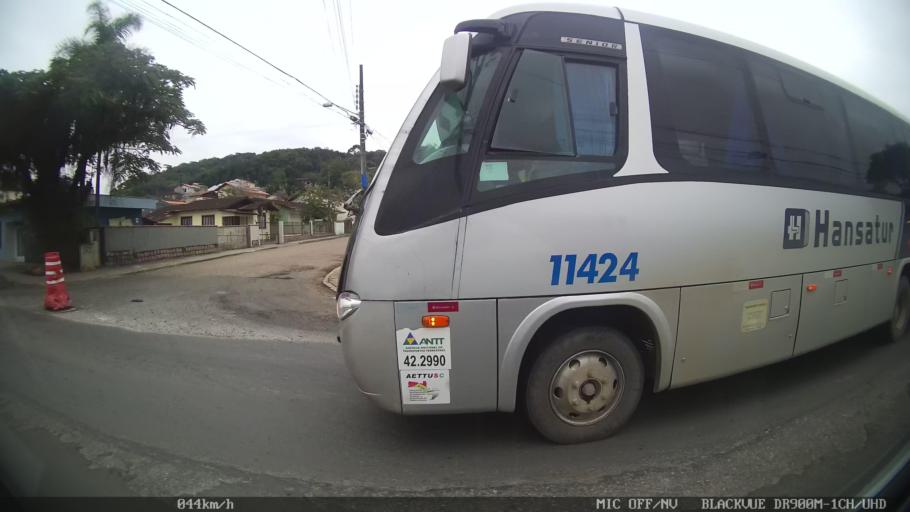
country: BR
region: Santa Catarina
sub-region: Joinville
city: Joinville
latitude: -26.2995
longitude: -48.8226
